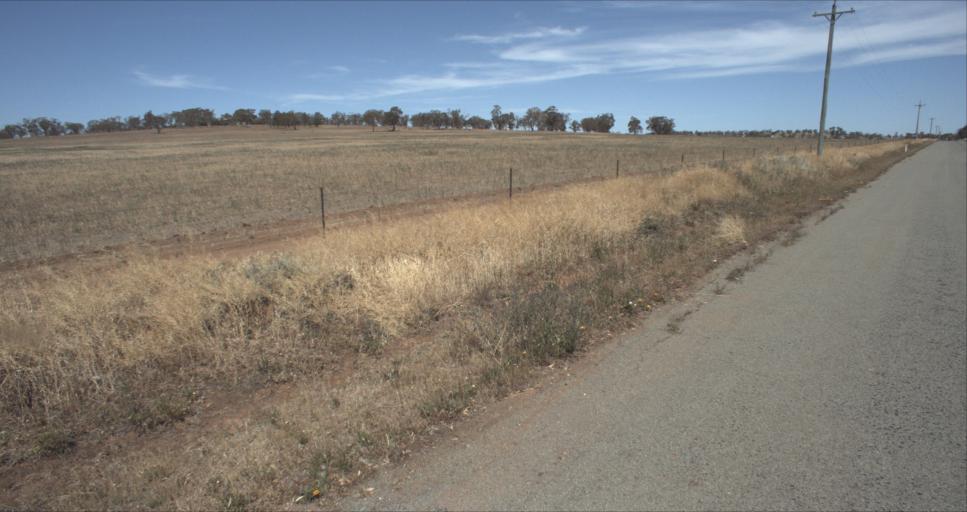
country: AU
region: New South Wales
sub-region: Leeton
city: Leeton
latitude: -34.6077
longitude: 146.4351
